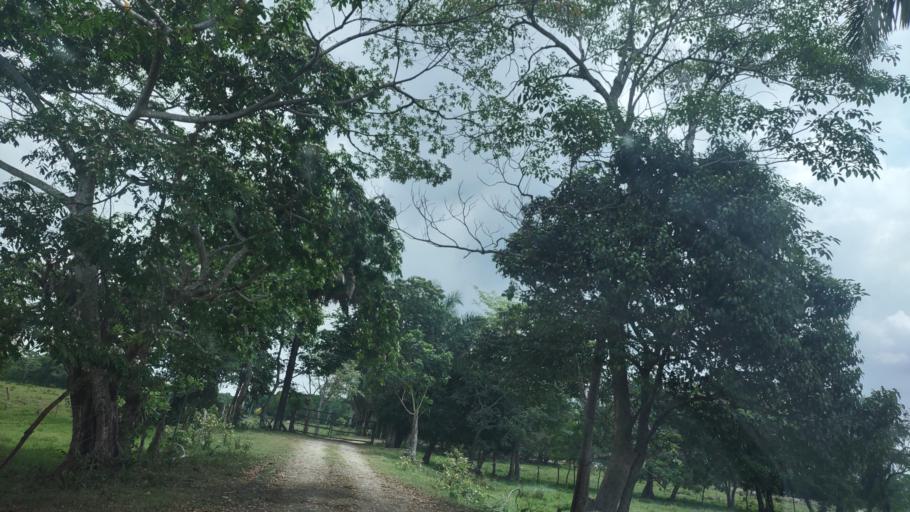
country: MX
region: Veracruz
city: Las Choapas
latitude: 17.9662
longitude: -94.1244
